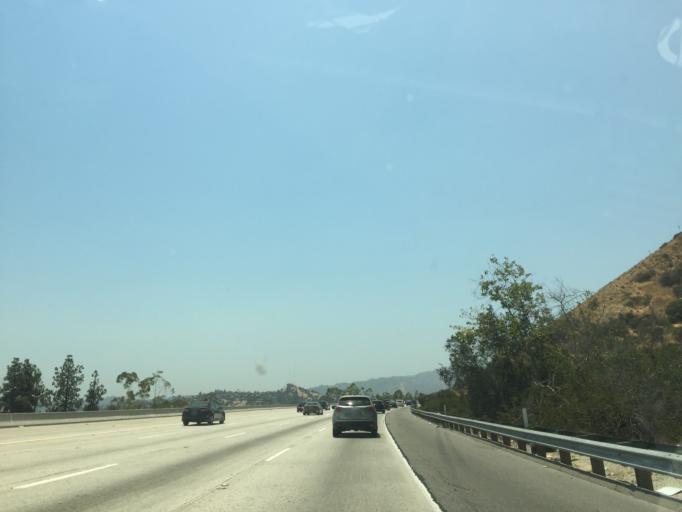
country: US
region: California
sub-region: Los Angeles County
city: Glendale
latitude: 34.1461
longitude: -118.2058
